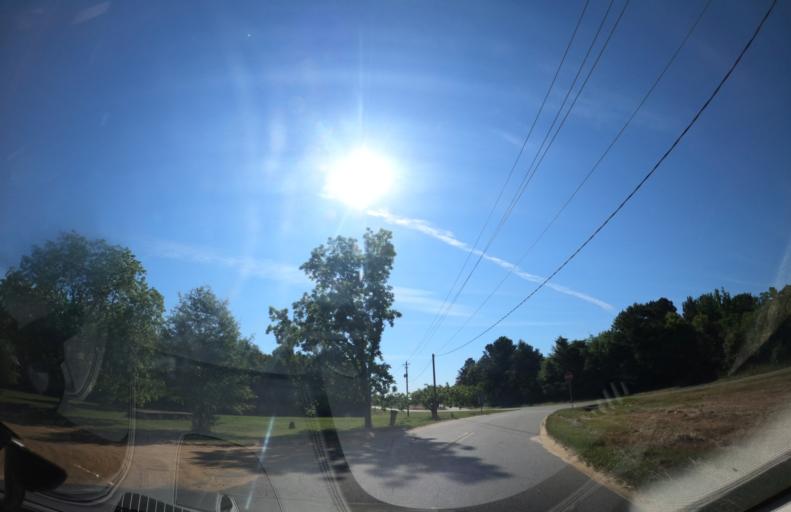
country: US
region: Georgia
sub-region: Jefferson County
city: Wrens
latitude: 33.2107
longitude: -82.3605
